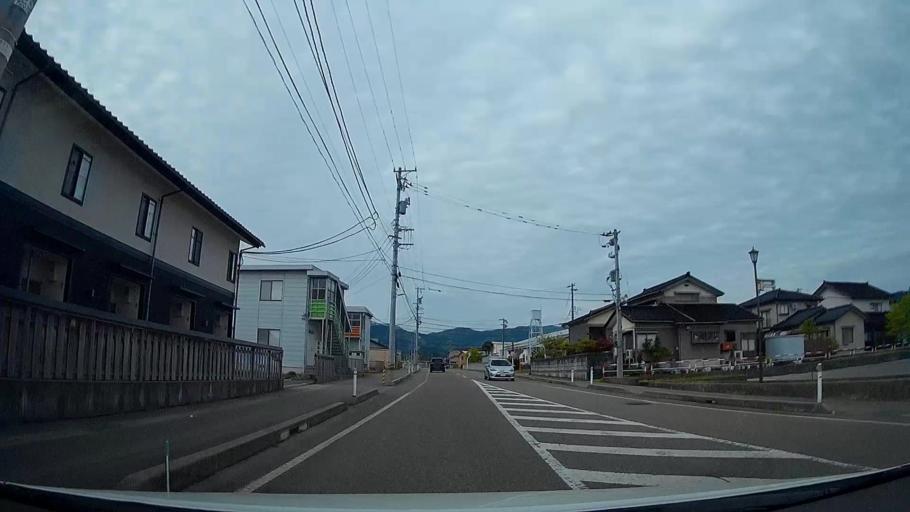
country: JP
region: Toyama
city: Fukumitsu
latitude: 36.5176
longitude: 136.8986
